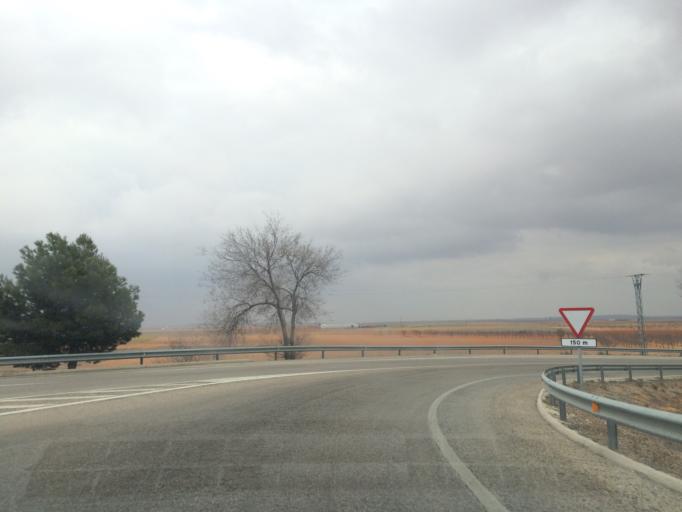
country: ES
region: Castille-La Mancha
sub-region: Province of Toledo
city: Madridejos
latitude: 39.4789
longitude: -3.5224
